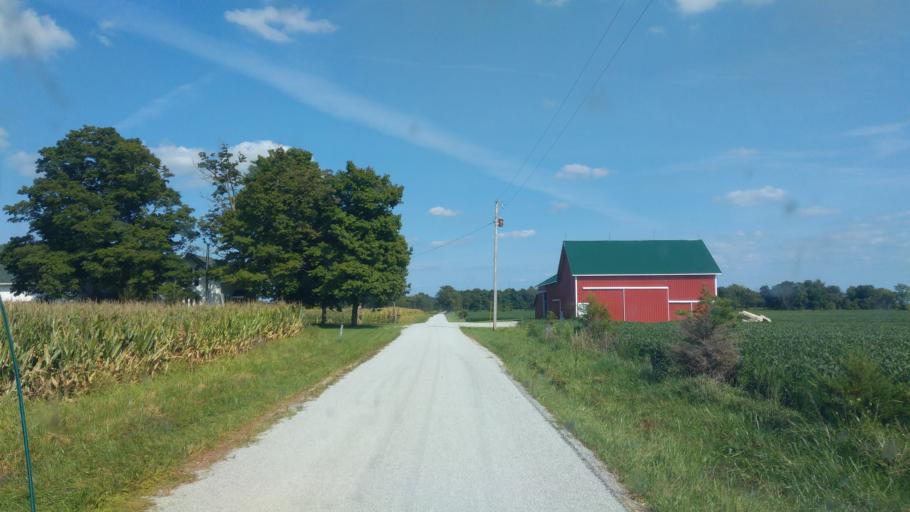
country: US
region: Ohio
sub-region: Hardin County
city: Kenton
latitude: 40.6292
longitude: -83.4520
